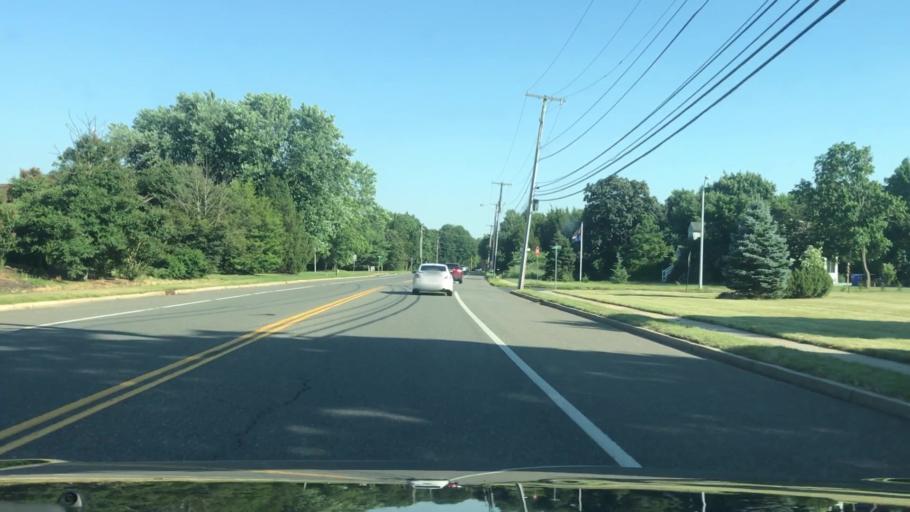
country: US
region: New Jersey
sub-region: Ocean County
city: Silver Ridge
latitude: 39.9977
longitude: -74.1981
